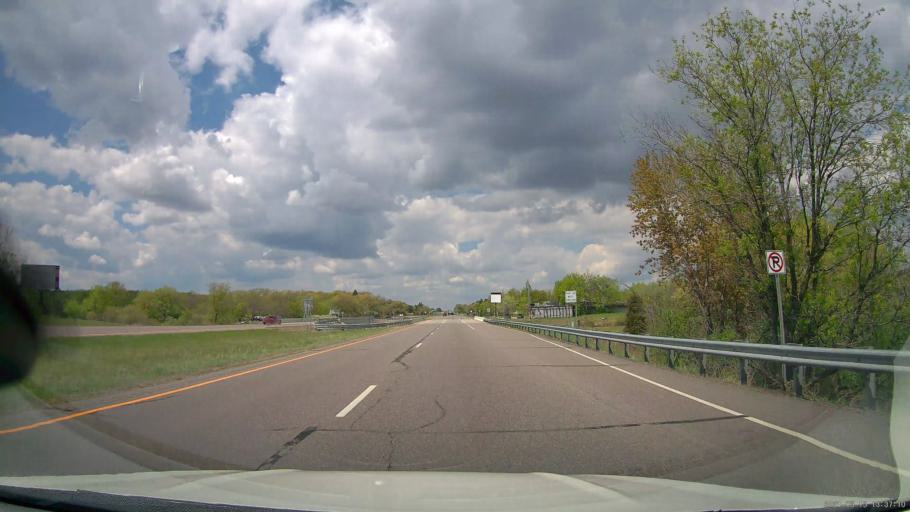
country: US
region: Minnesota
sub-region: Benton County
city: Rice
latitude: 45.7040
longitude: -94.1737
